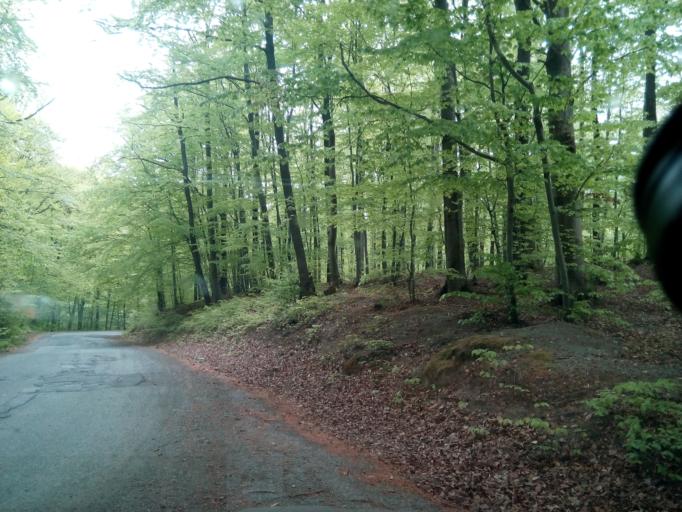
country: SK
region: Kosicky
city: Secovce
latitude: 48.8078
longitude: 21.5135
